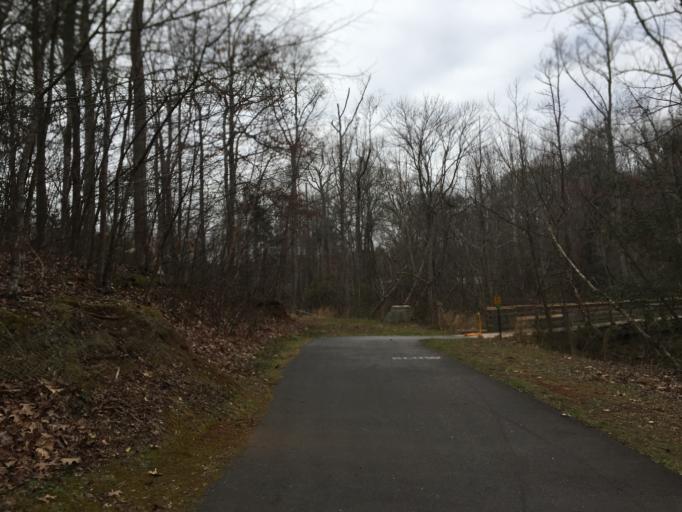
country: US
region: South Carolina
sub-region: Greenville County
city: Mauldin
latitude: 34.7743
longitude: -82.3626
